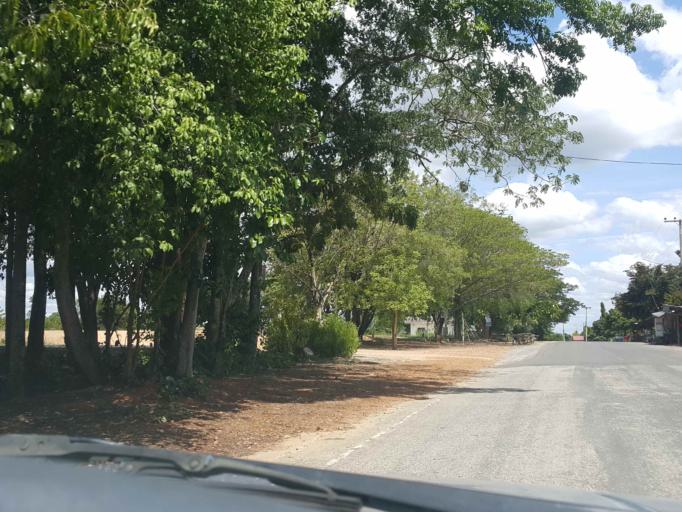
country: TH
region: Chiang Mai
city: Doi Lo
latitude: 18.4687
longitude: 98.7597
